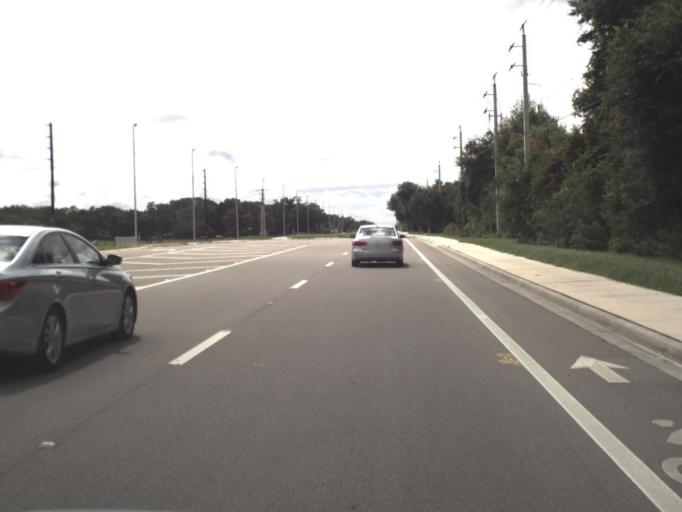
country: US
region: Florida
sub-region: Manatee County
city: Ellenton
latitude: 27.5667
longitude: -82.4309
